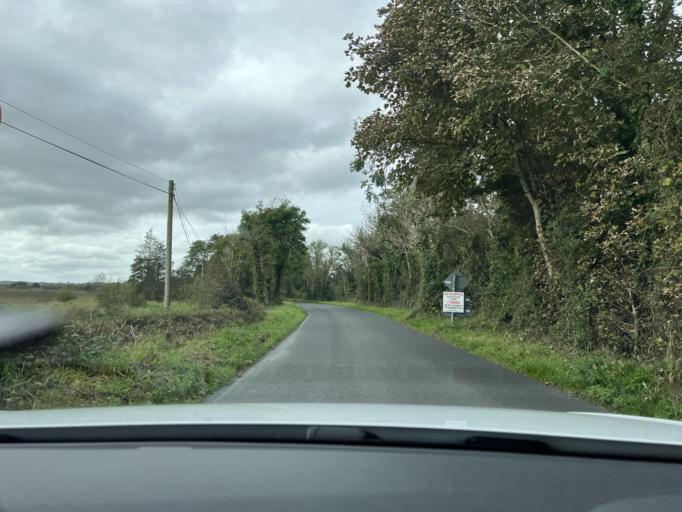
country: IE
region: Connaught
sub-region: County Leitrim
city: Carrick-on-Shannon
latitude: 53.9665
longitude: -8.0892
